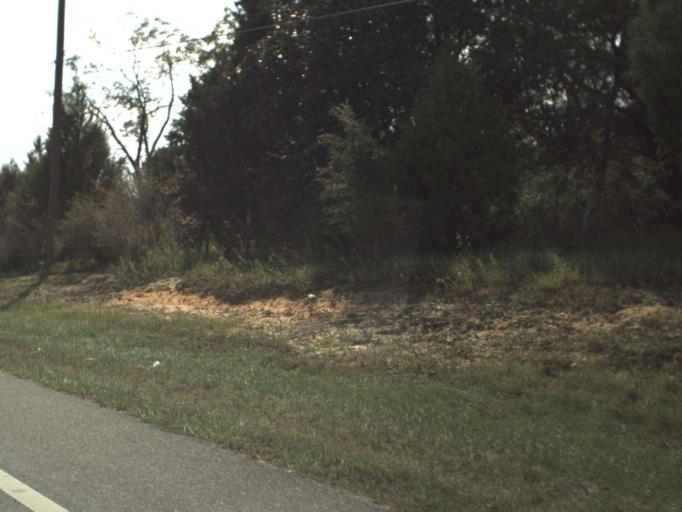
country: US
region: Florida
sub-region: Holmes County
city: Bonifay
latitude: 30.7347
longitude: -85.6854
